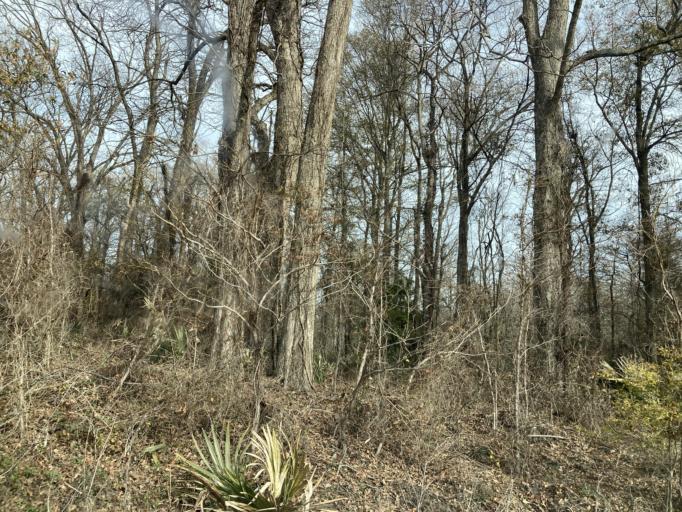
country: US
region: Mississippi
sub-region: Humphreys County
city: Belzoni
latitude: 33.0667
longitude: -90.6146
